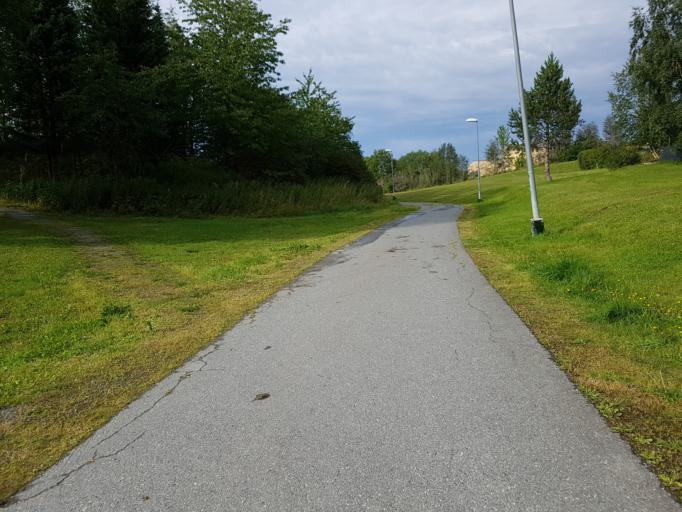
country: NO
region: Sor-Trondelag
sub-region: Trondheim
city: Trondheim
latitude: 63.3954
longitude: 10.4321
